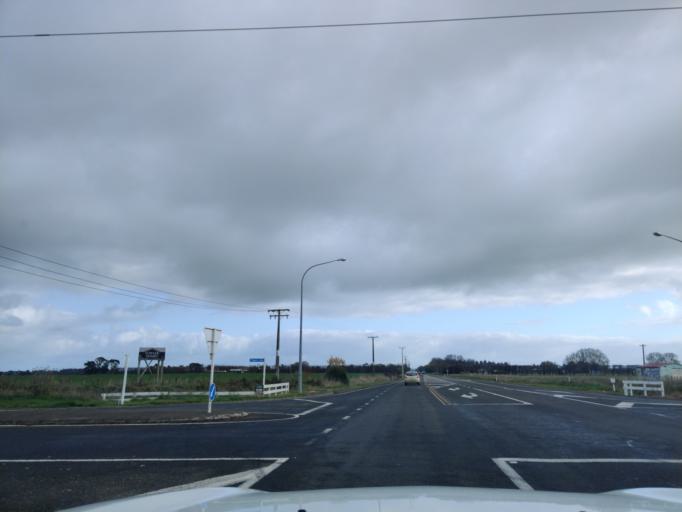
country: NZ
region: Manawatu-Wanganui
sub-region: Palmerston North City
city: Palmerston North
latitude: -40.3329
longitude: 175.5905
